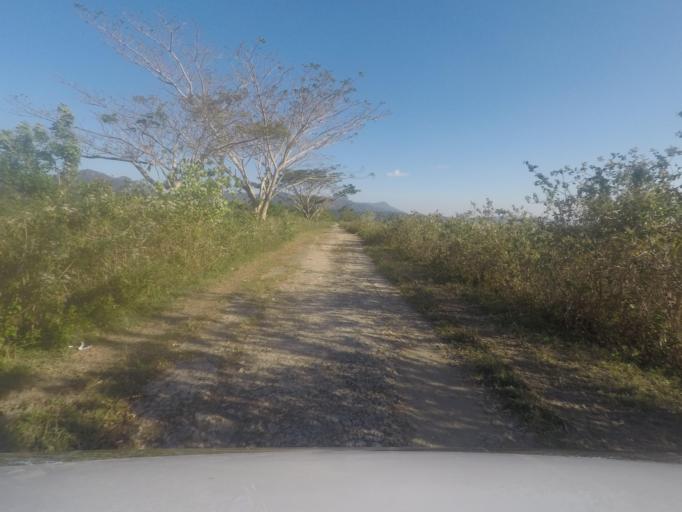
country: TL
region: Lautem
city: Lospalos
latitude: -8.4071
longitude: 127.1983
